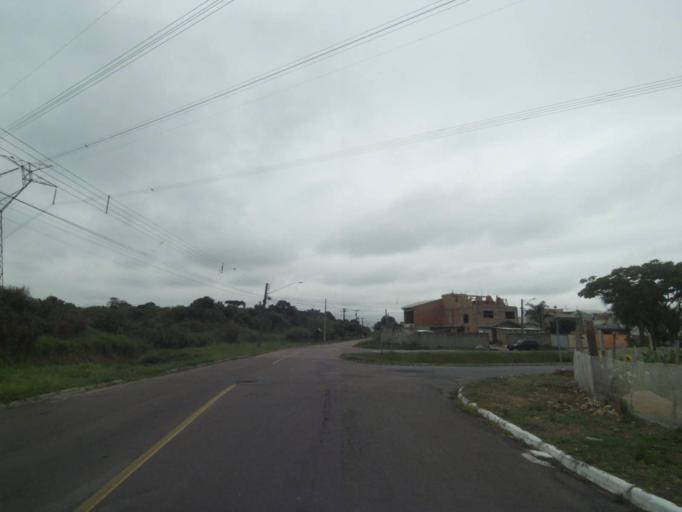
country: BR
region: Parana
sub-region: Araucaria
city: Araucaria
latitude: -25.5437
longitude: -49.3448
